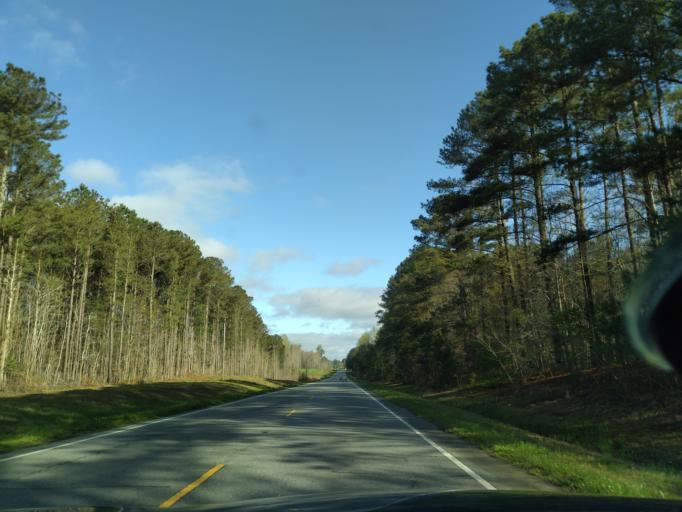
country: US
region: North Carolina
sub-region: Washington County
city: Plymouth
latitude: 36.0219
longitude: -76.7802
